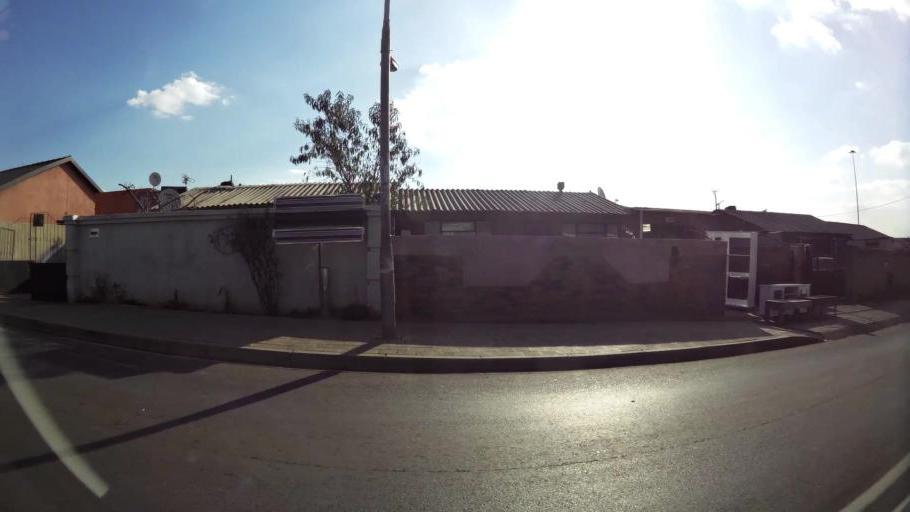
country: ZA
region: Gauteng
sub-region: City of Johannesburg Metropolitan Municipality
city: Soweto
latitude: -26.2585
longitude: 27.9151
